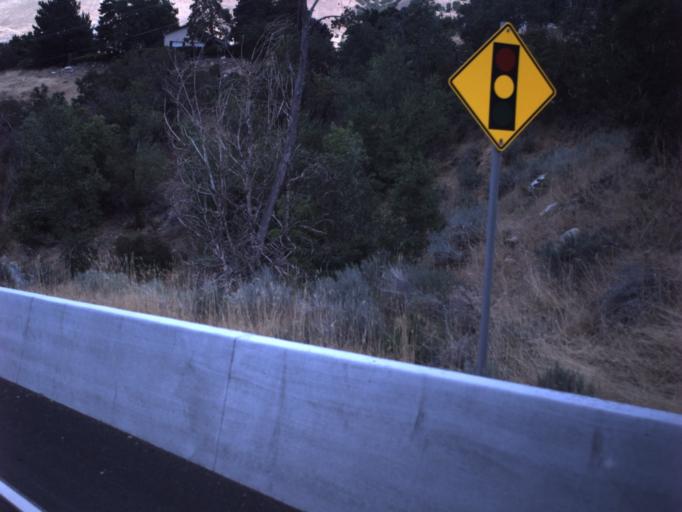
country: US
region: Utah
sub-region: Salt Lake County
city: Cottonwood Heights
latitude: 40.6171
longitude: -111.7890
